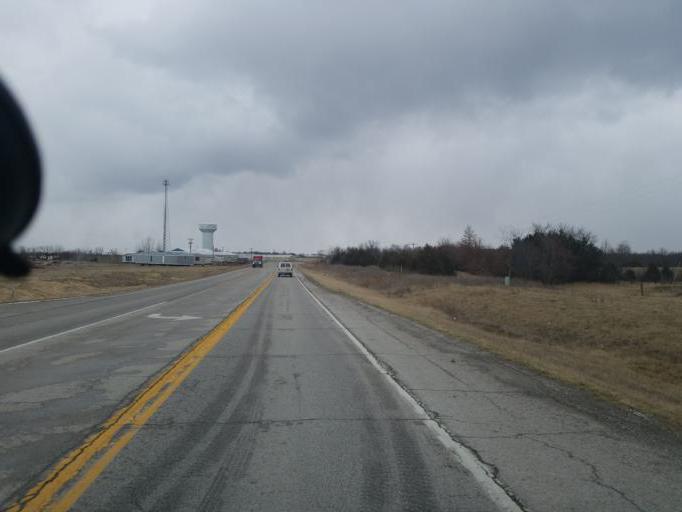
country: US
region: Missouri
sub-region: Macon County
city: Macon
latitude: 39.7664
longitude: -92.4696
